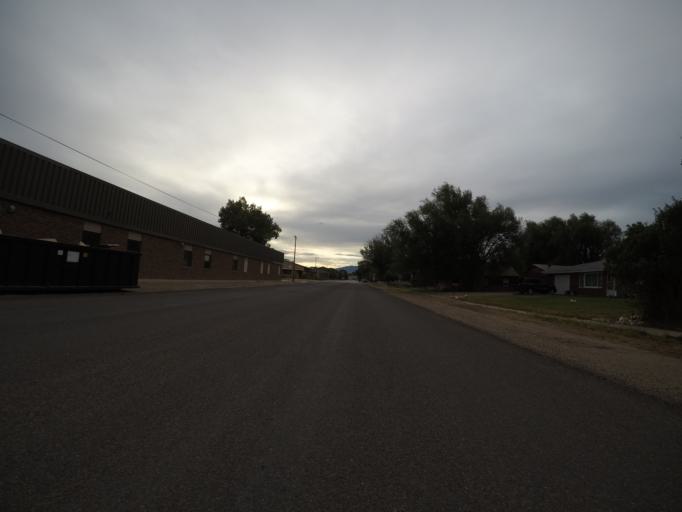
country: US
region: Wyoming
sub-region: Carbon County
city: Saratoga
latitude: 41.4530
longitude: -106.8118
